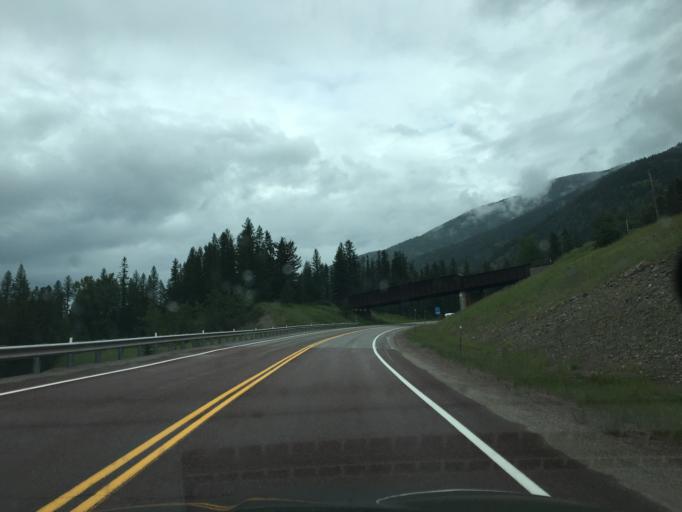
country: US
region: Montana
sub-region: Flathead County
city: Bigfork
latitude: 48.2378
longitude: -113.5695
